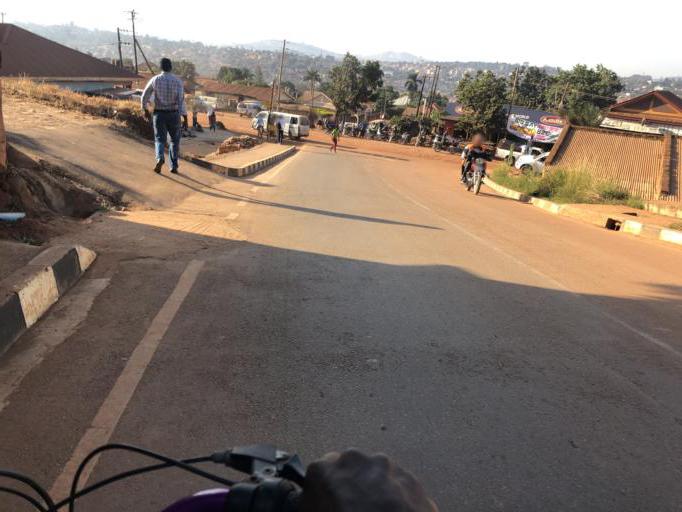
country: UG
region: Central Region
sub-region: Kampala District
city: Kampala
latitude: 0.2794
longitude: 32.5983
